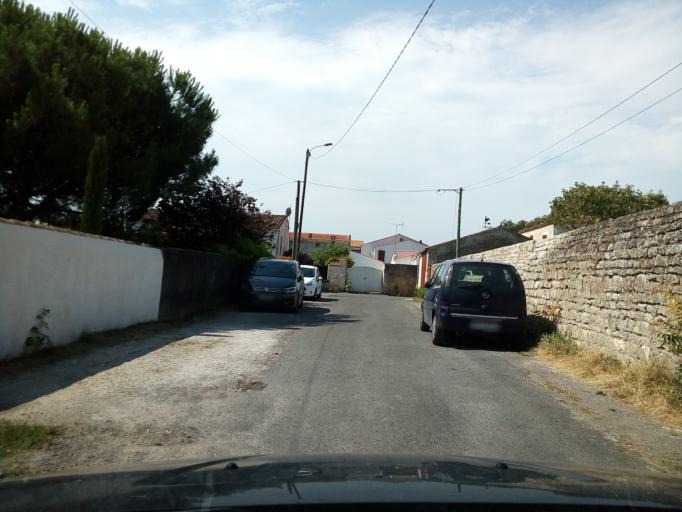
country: FR
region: Poitou-Charentes
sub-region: Departement de la Charente-Maritime
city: Dolus-d'Oleron
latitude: 45.9444
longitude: -1.3028
